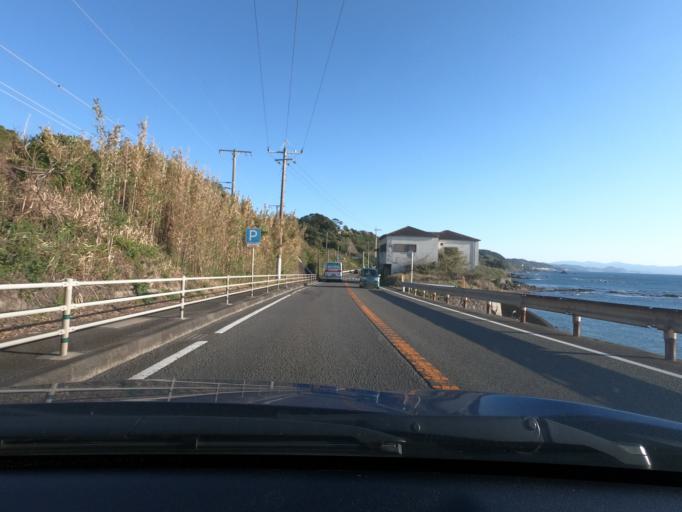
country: JP
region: Kagoshima
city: Akune
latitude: 31.9726
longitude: 130.2089
